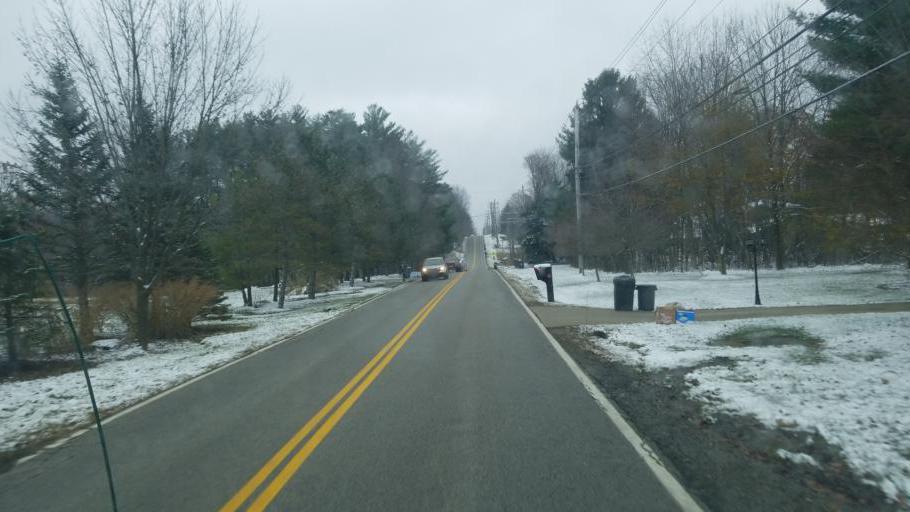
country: US
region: Ohio
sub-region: Cuyahoga County
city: Brecksville
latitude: 41.2895
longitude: -81.6508
